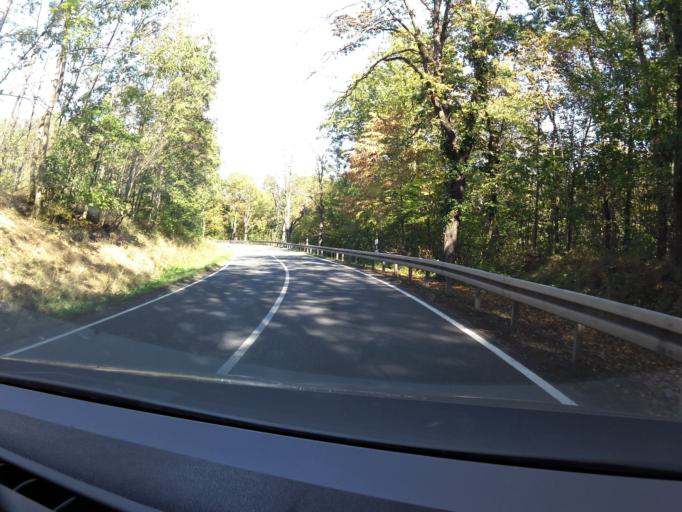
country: DE
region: Saxony-Anhalt
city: Gernrode
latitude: 51.7192
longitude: 11.1423
